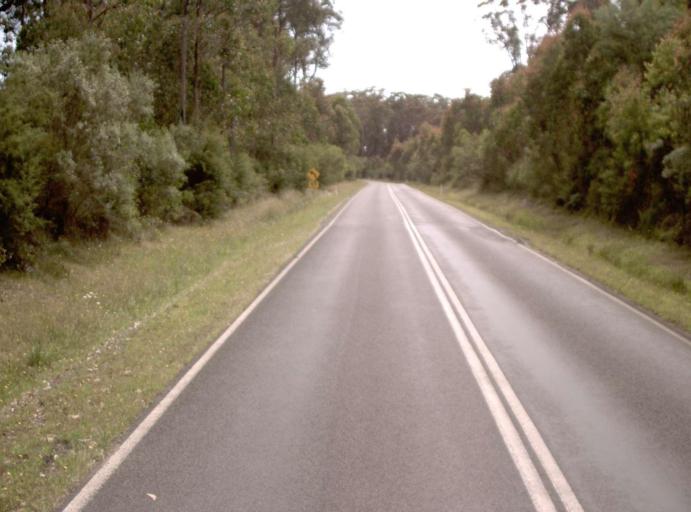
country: AU
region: Victoria
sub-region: Latrobe
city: Morwell
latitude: -38.0635
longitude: 146.4222
